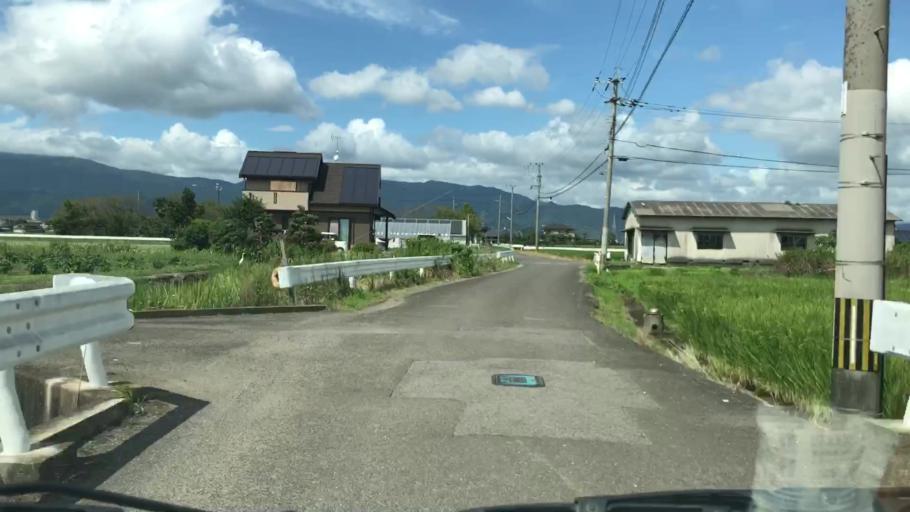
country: JP
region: Saga Prefecture
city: Saga-shi
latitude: 33.2366
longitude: 130.2120
